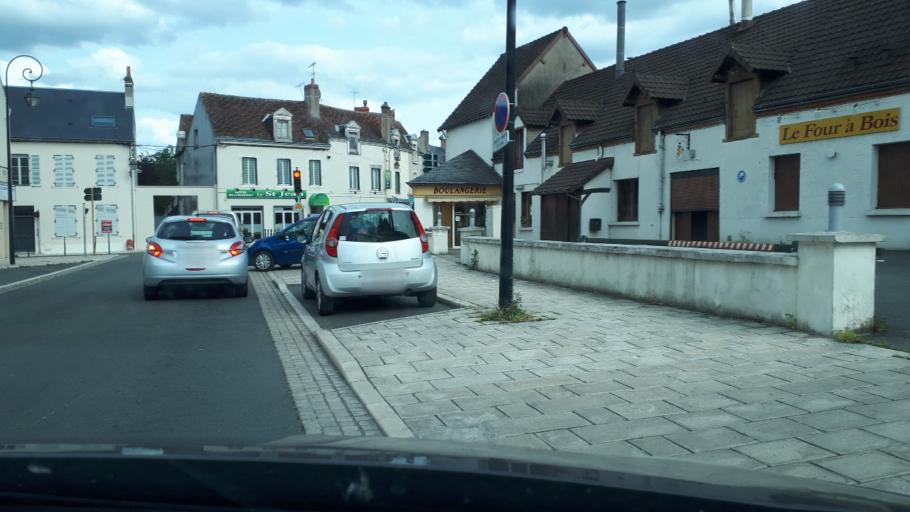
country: FR
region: Centre
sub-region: Departement du Loir-et-Cher
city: Romorantin-Lanthenay
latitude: 47.3549
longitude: 1.7420
